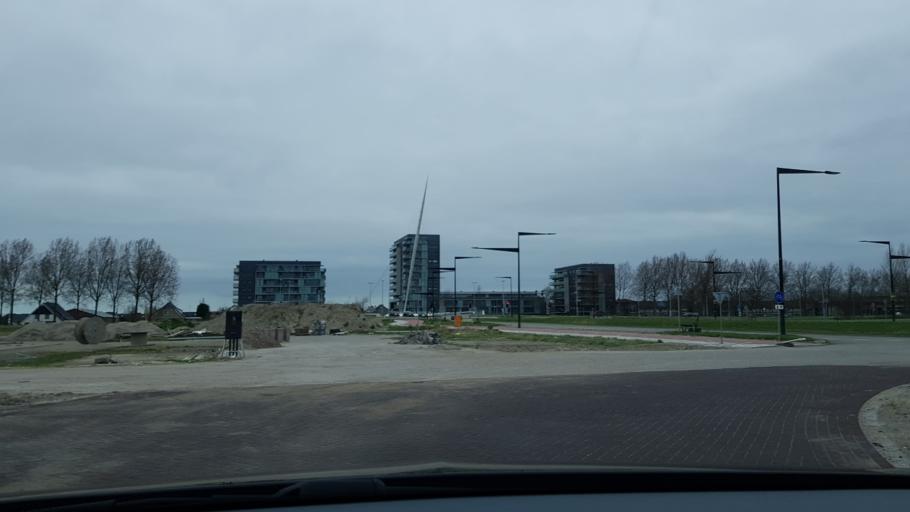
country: NL
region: North Holland
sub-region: Gemeente Haarlemmermeer
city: Hoofddorp
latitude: 52.2890
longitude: 4.6733
